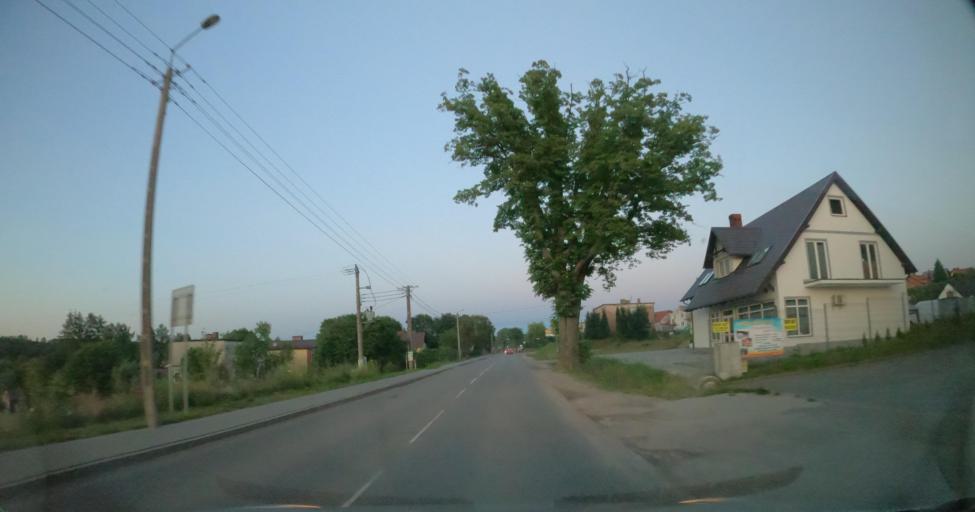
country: PL
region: Pomeranian Voivodeship
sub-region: Powiat wejherowski
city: Szemud
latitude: 54.4864
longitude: 18.2289
